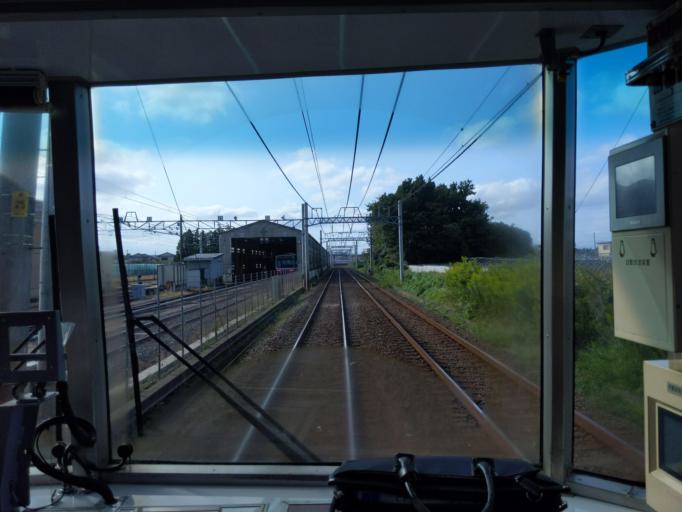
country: JP
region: Chiba
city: Kashiwa
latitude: 35.7780
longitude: 139.9802
